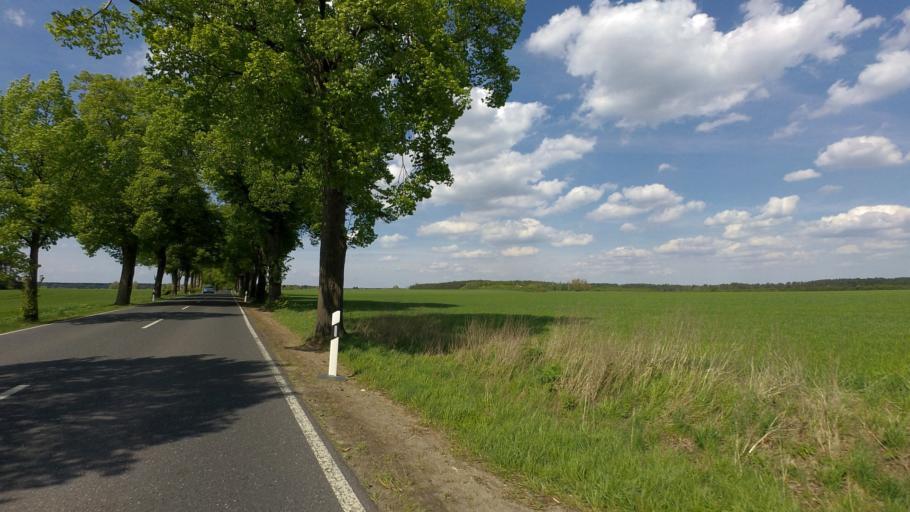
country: DE
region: Brandenburg
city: Marienwerder
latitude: 52.8908
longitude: 13.5427
